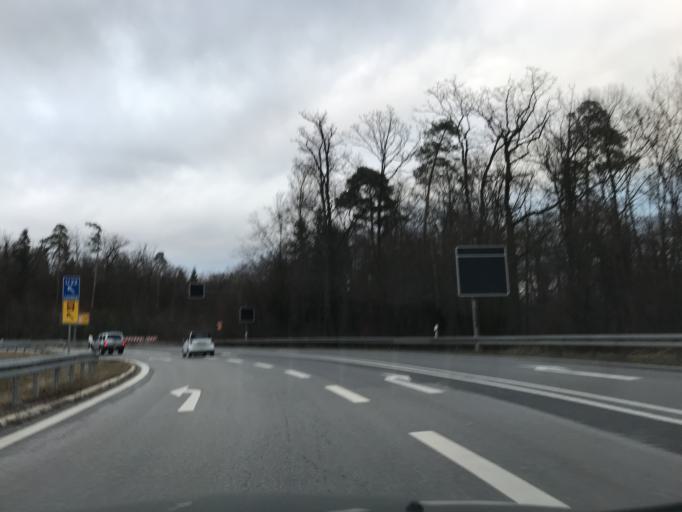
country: DE
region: Baden-Wuerttemberg
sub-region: Regierungsbezirk Stuttgart
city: Stuttgart
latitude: 48.7576
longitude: 9.1168
